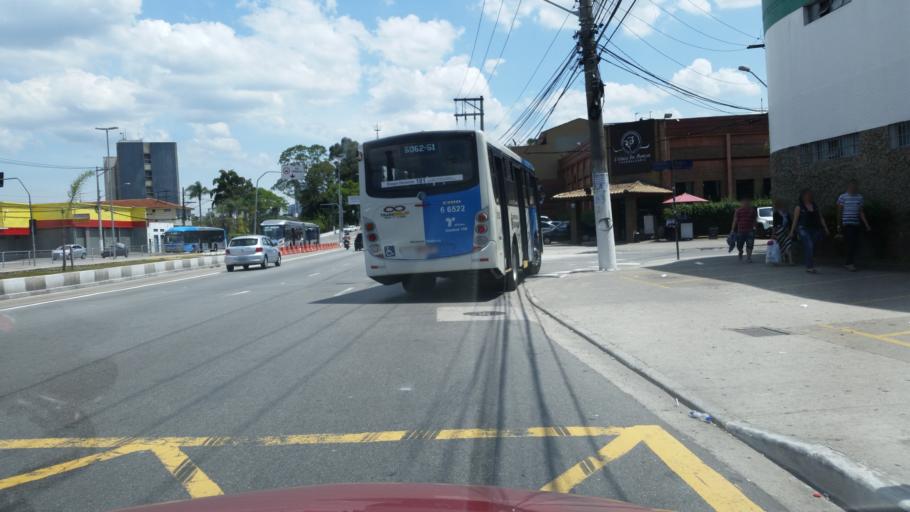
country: BR
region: Sao Paulo
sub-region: Diadema
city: Diadema
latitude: -23.6631
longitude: -46.7077
